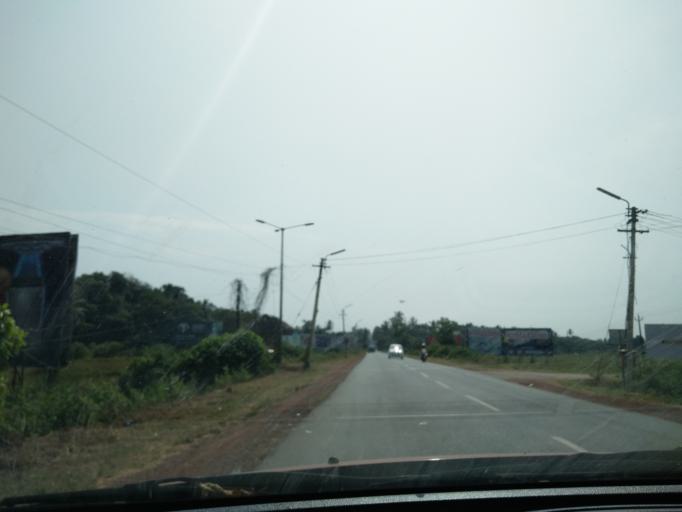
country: IN
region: Goa
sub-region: South Goa
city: Raia
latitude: 15.3014
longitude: 73.9495
